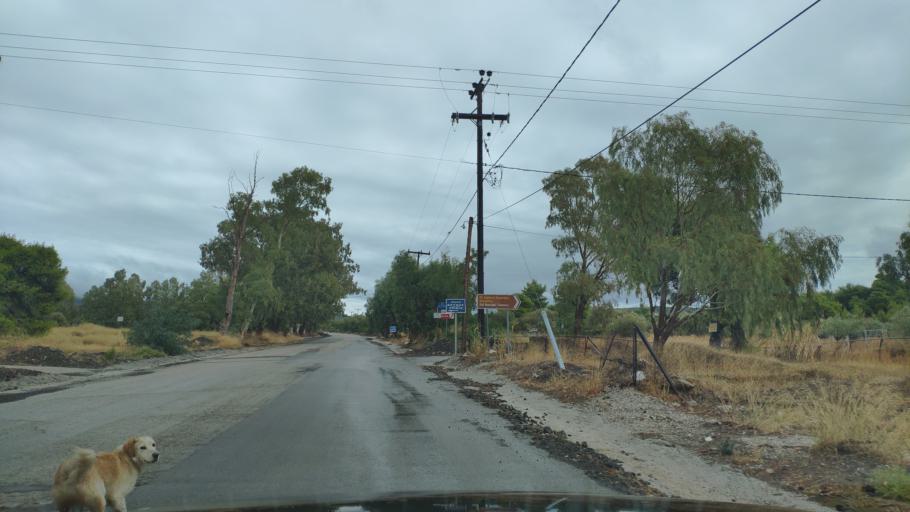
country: GR
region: Peloponnese
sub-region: Nomos Korinthias
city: Loutraki
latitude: 37.9647
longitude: 23.0004
